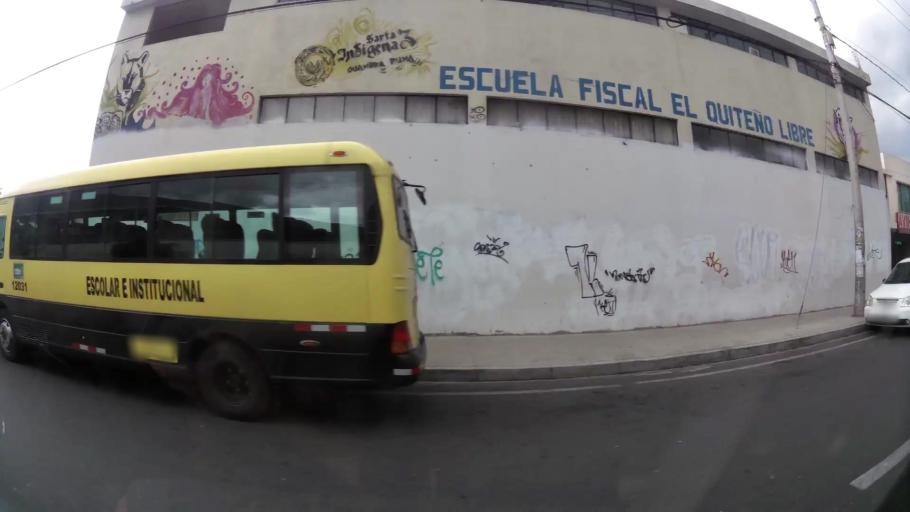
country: EC
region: Pichincha
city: Quito
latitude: -0.0531
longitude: -78.4558
